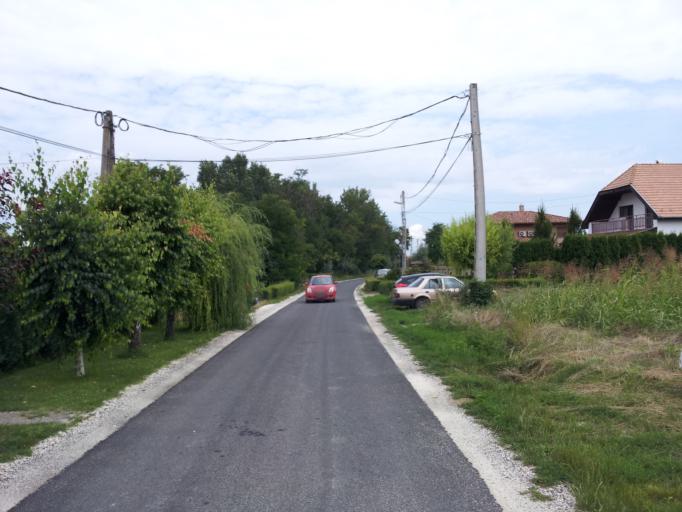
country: HU
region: Pest
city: Rackeve
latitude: 47.1821
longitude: 18.9545
